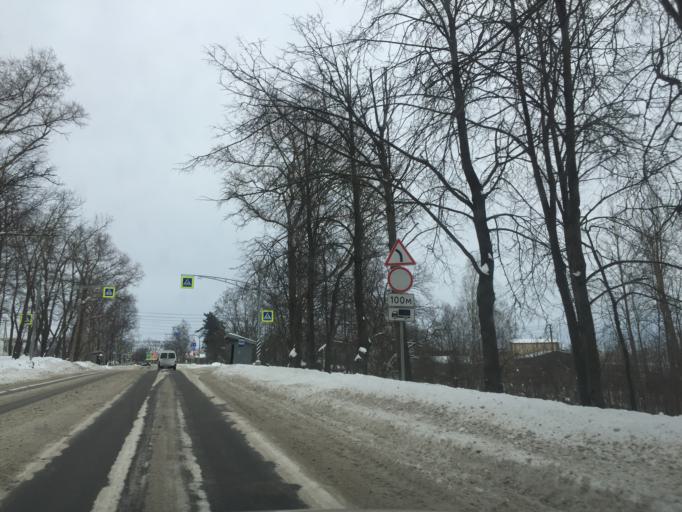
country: RU
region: Leningrad
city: Yanino Vtoroye
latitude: 59.9299
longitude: 30.6183
